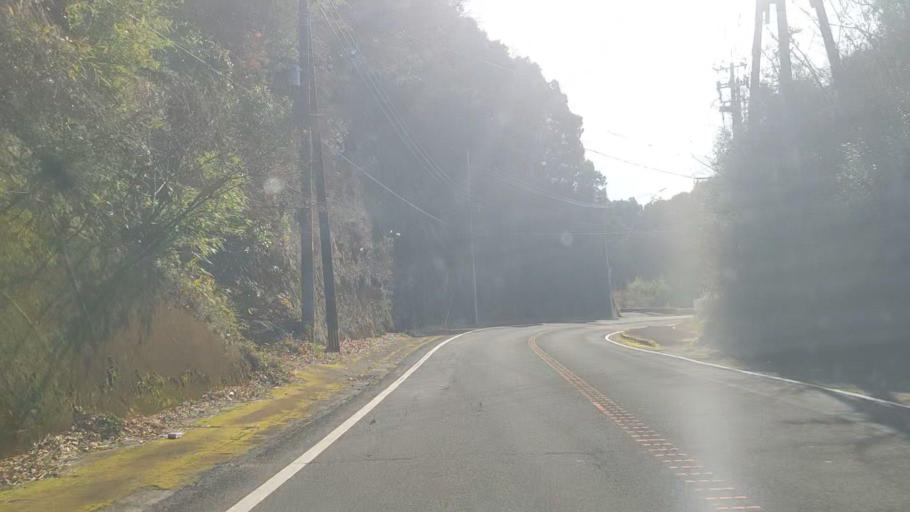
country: JP
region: Kagoshima
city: Okuchi-shinohara
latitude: 31.9372
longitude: 130.7056
